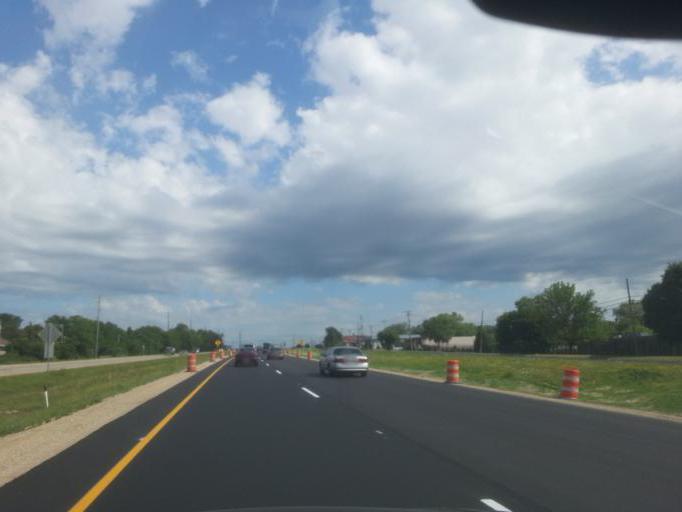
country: US
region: Wisconsin
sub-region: Dane County
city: Monona
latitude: 43.0571
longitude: -89.3092
